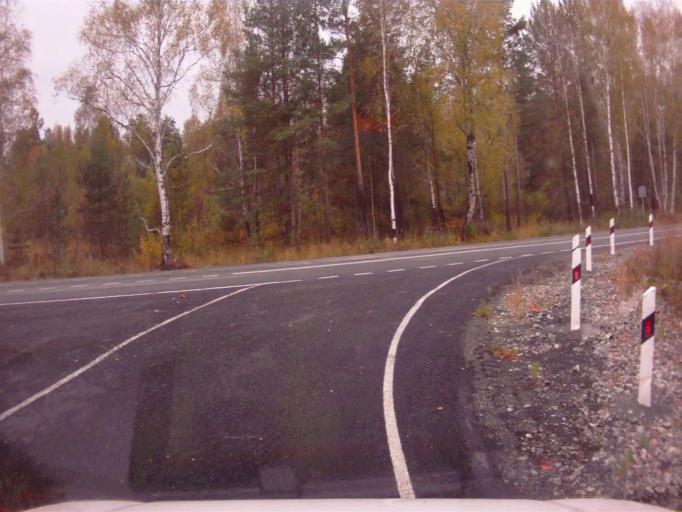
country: RU
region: Chelyabinsk
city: Nyazepetrovsk
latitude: 56.0434
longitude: 59.7741
